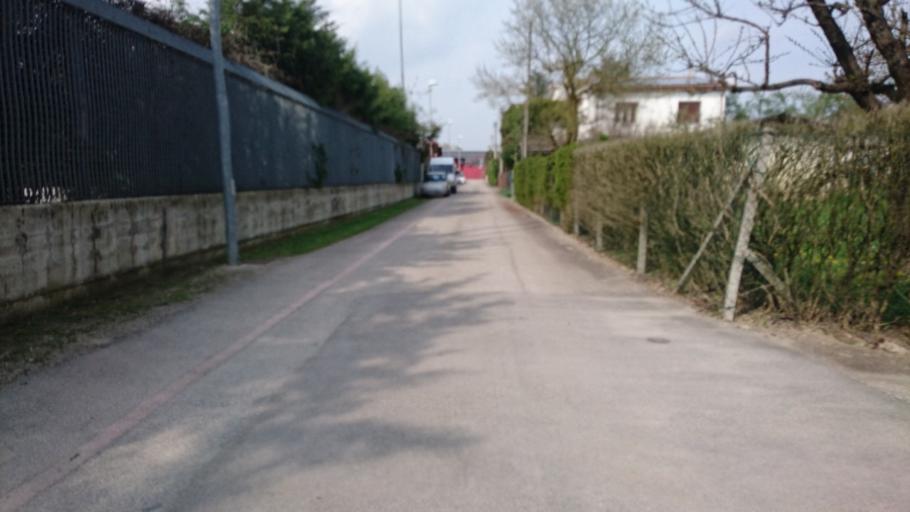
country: IT
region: Veneto
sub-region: Provincia di Padova
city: Noventa
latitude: 45.4106
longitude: 11.9363
